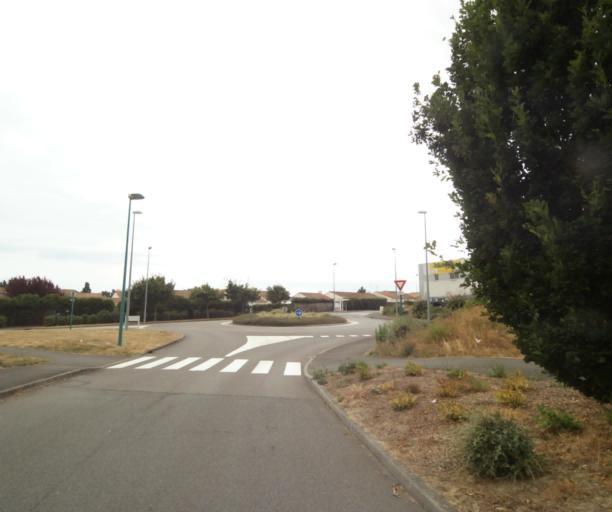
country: FR
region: Pays de la Loire
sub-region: Departement de la Vendee
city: Chateau-d'Olonne
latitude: 46.4932
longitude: -1.7474
